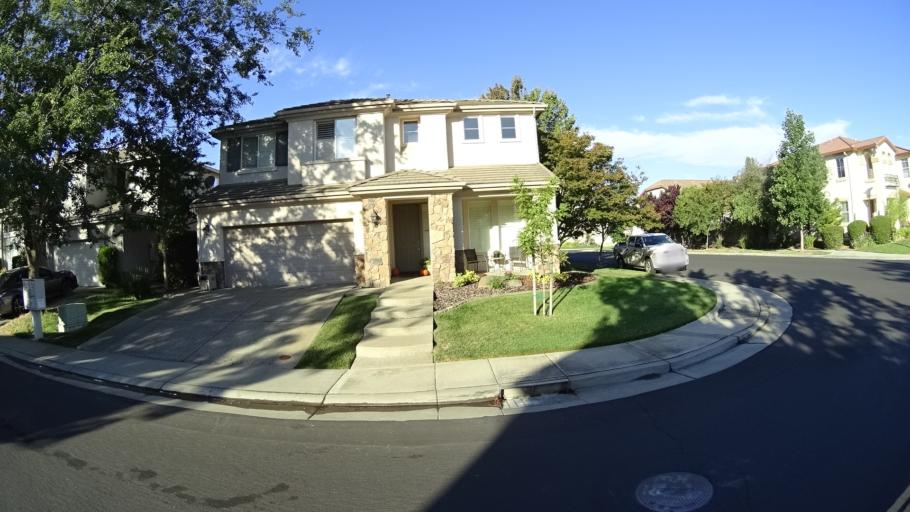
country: US
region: California
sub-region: Sacramento County
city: Laguna
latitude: 38.4023
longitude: -121.4776
